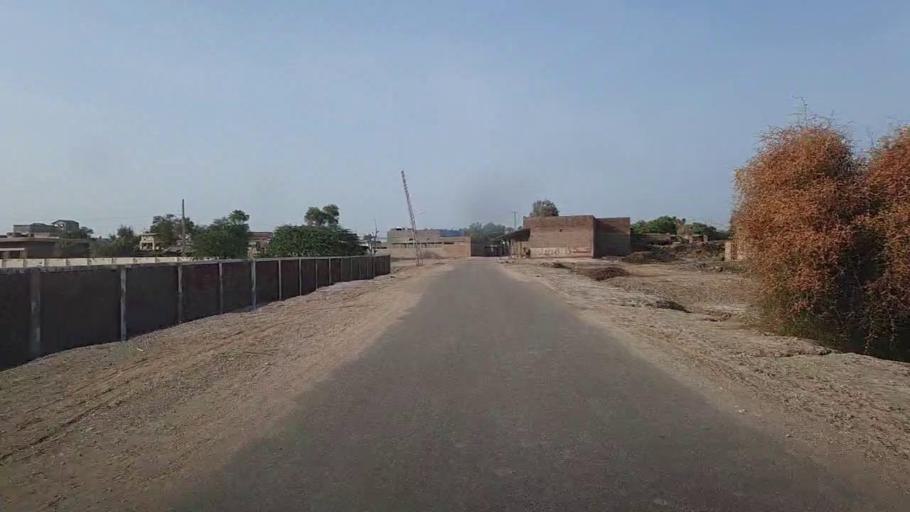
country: PK
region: Sindh
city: Ubauro
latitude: 28.1025
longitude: 69.8453
